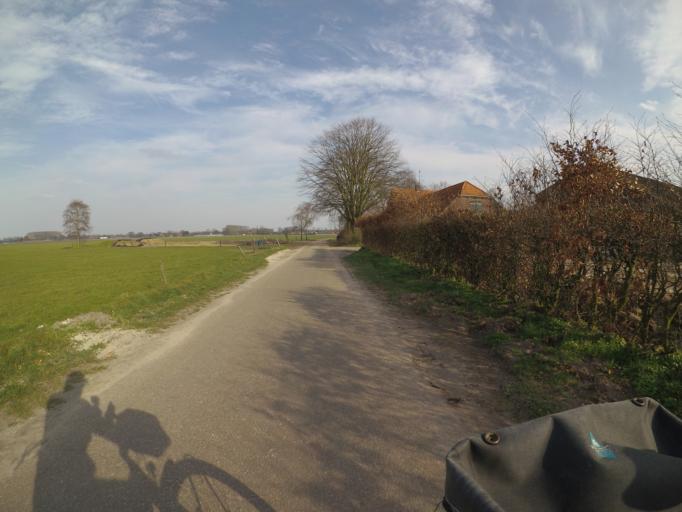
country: NL
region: North Brabant
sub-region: Gemeente Dongen
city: Dongen
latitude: 51.6018
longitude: 4.9070
